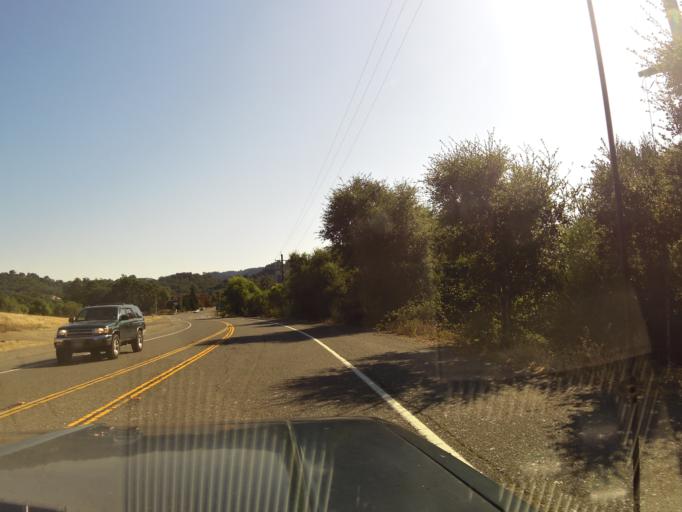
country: US
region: California
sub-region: Sonoma County
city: Cloverdale
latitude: 38.8277
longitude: -123.0152
